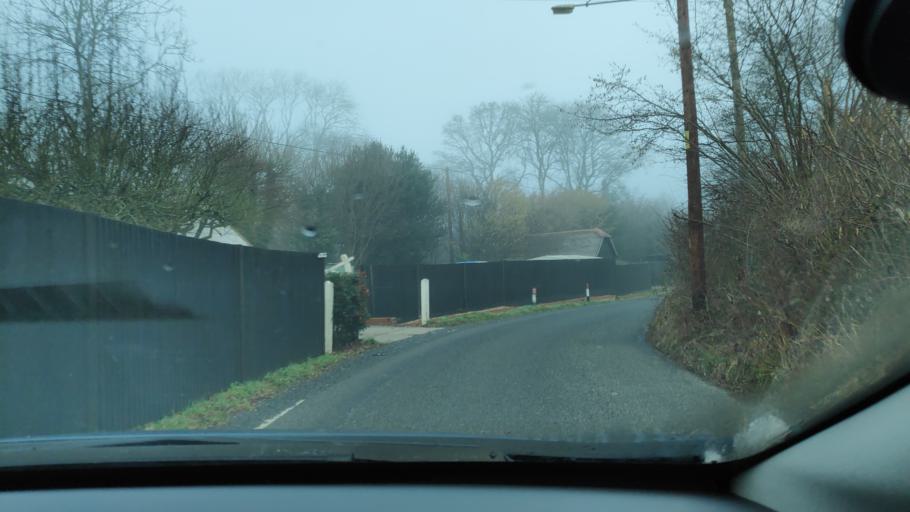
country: GB
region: England
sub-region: Surrey
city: Seale
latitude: 51.2470
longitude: -0.7050
